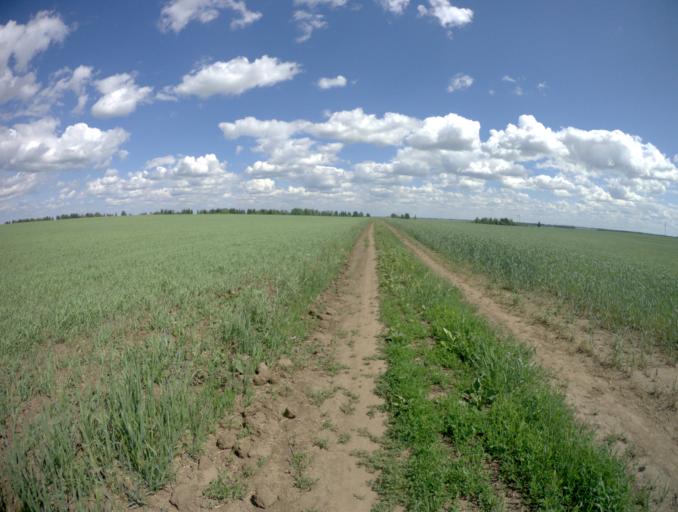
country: RU
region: Vladimir
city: Suzdal'
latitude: 56.4350
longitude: 40.3400
